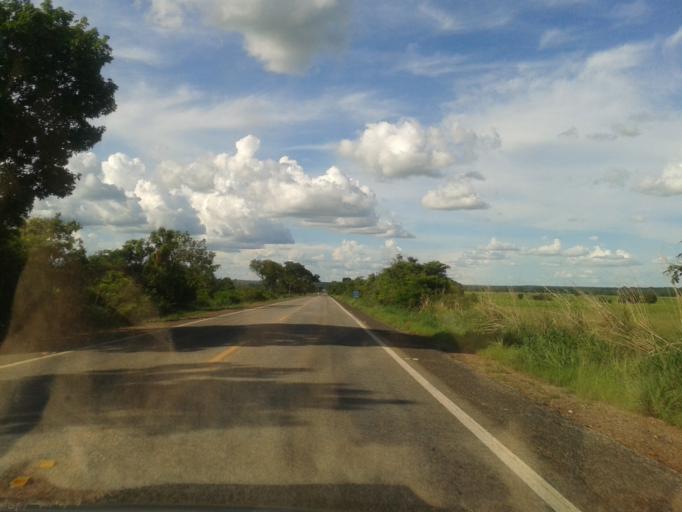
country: BR
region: Goias
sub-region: Mozarlandia
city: Mozarlandia
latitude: -14.5195
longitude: -50.4855
